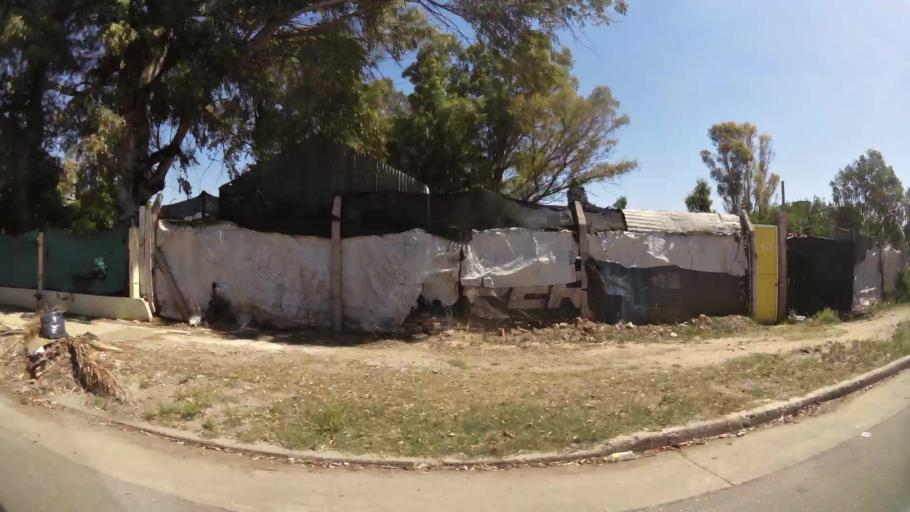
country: AR
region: Cordoba
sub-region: Departamento de Capital
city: Cordoba
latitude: -31.3912
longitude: -64.1886
